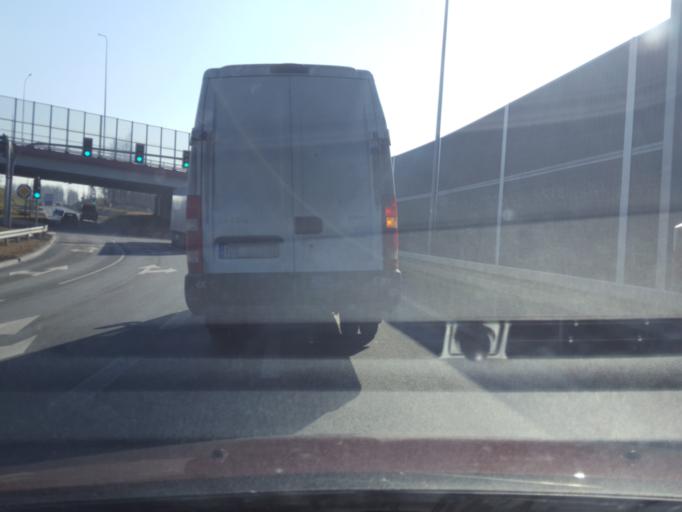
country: PL
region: Lesser Poland Voivodeship
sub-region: Powiat wielicki
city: Kokotow
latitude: 50.0624
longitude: 20.0724
